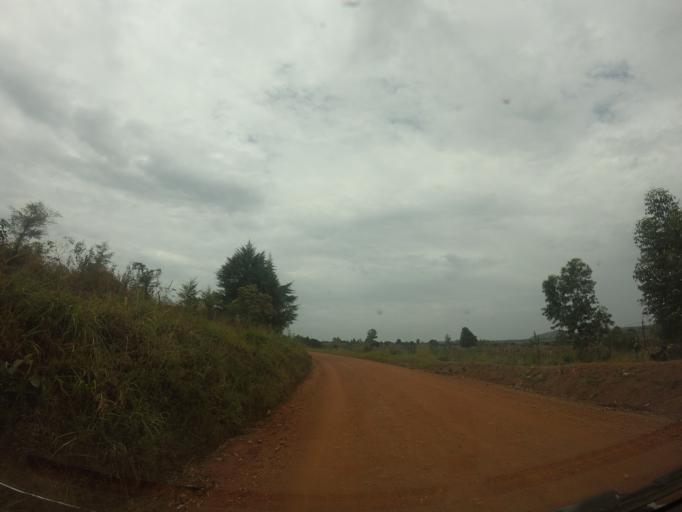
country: UG
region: Northern Region
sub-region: Arua District
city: Arua
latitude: 2.8473
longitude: 30.8893
